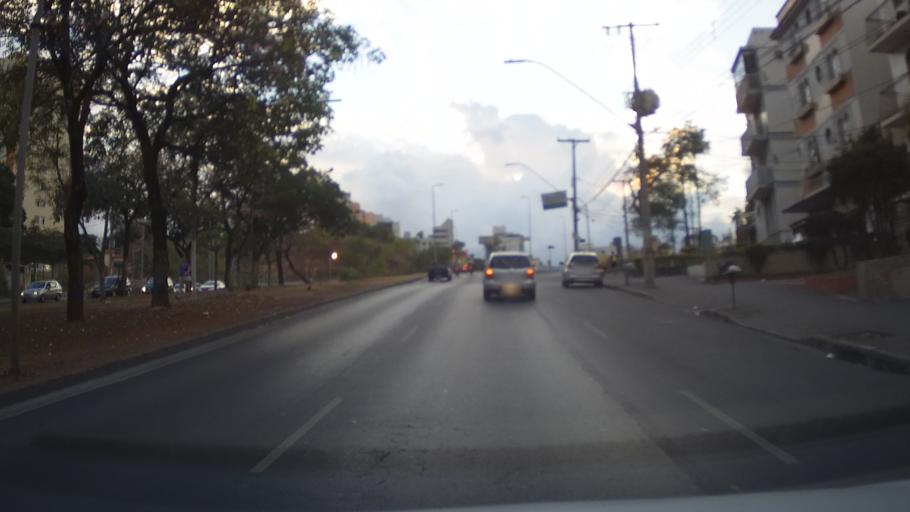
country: BR
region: Minas Gerais
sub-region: Belo Horizonte
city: Belo Horizonte
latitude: -19.8940
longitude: -43.9257
